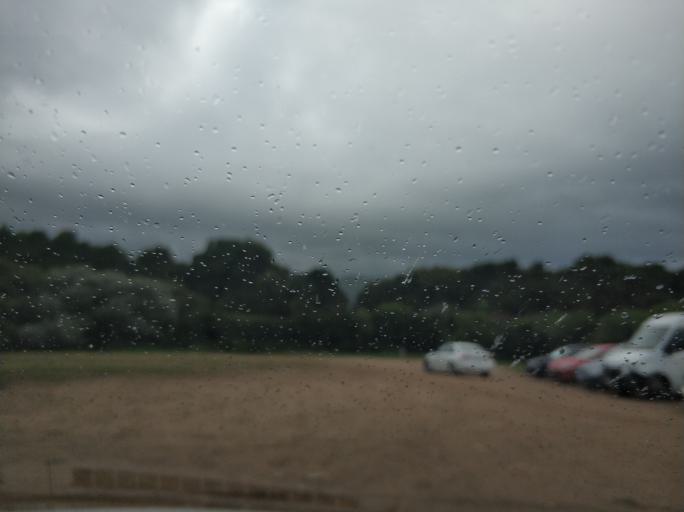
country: ES
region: Galicia
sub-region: Provincia de Lugo
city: Barreiros
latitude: 43.5531
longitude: -7.1592
